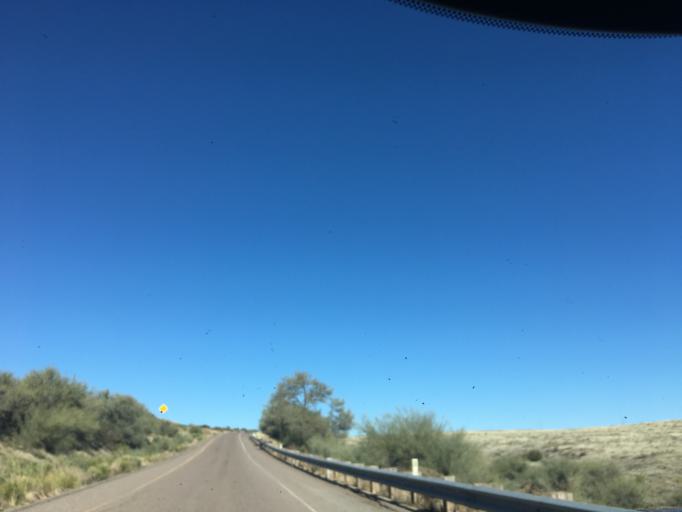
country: US
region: Arizona
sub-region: Yavapai County
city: Cordes Lakes
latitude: 34.1940
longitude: -112.1305
